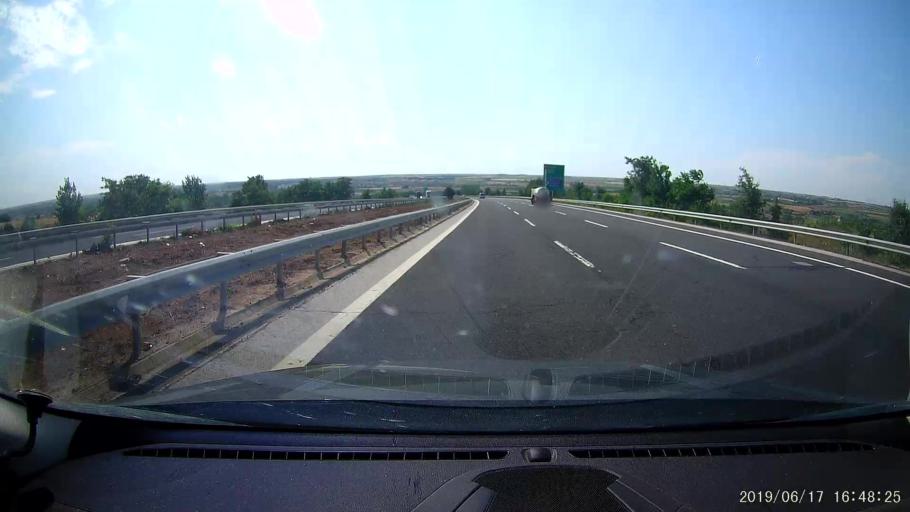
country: TR
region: Kirklareli
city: Babaeski
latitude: 41.5057
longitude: 27.1429
